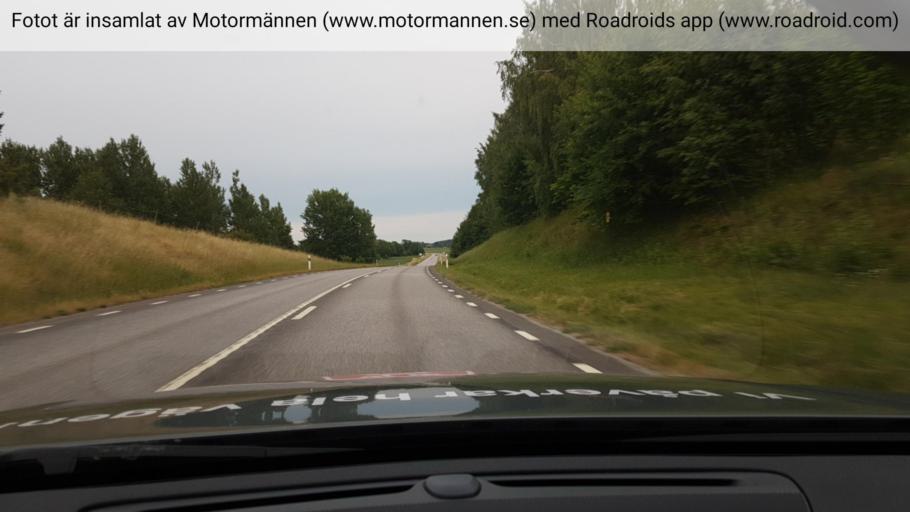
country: SE
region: OEstergoetland
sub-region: Motala Kommun
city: Borensberg
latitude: 58.5369
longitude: 15.3822
